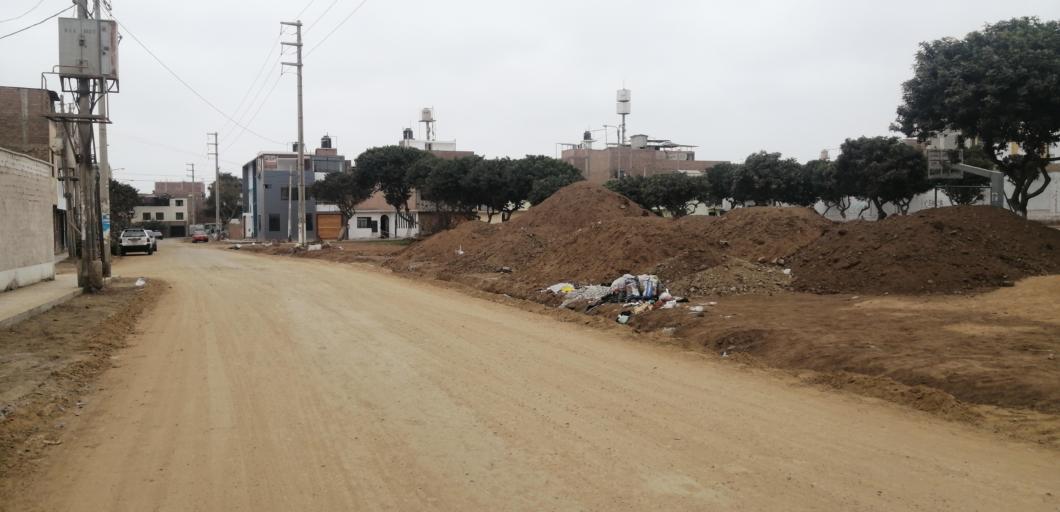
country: PE
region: La Libertad
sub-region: Provincia de Trujillo
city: Trujillo
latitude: -8.1045
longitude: -79.0443
